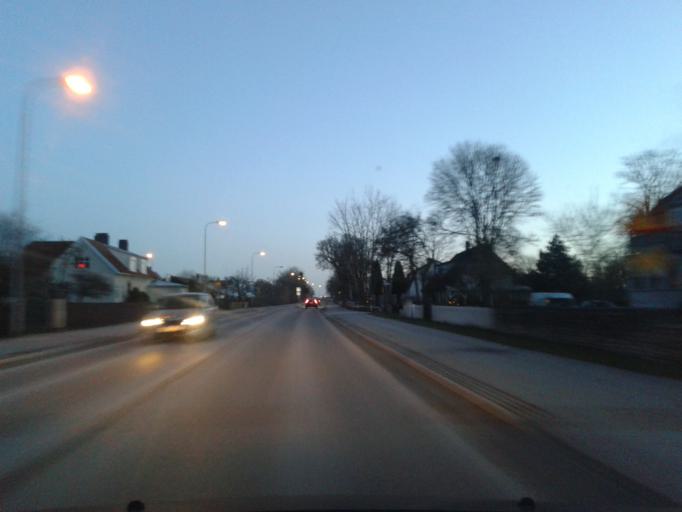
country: SE
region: Gotland
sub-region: Gotland
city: Visby
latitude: 57.6311
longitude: 18.3134
